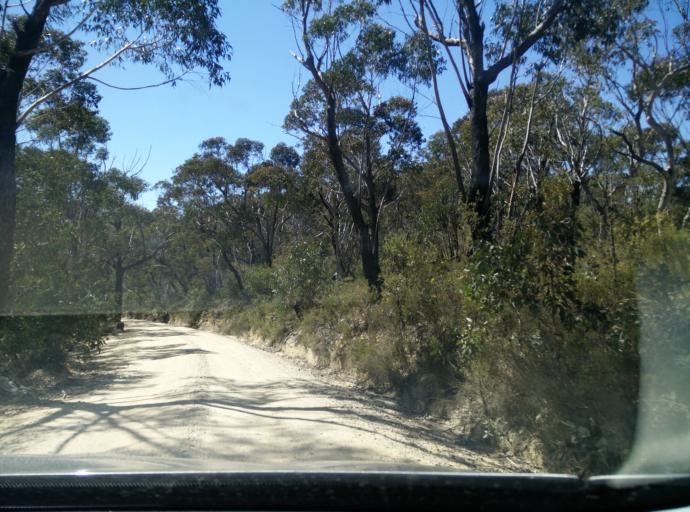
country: AU
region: New South Wales
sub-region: Blue Mountains Municipality
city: Blackheath
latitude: -33.5875
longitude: 150.2719
